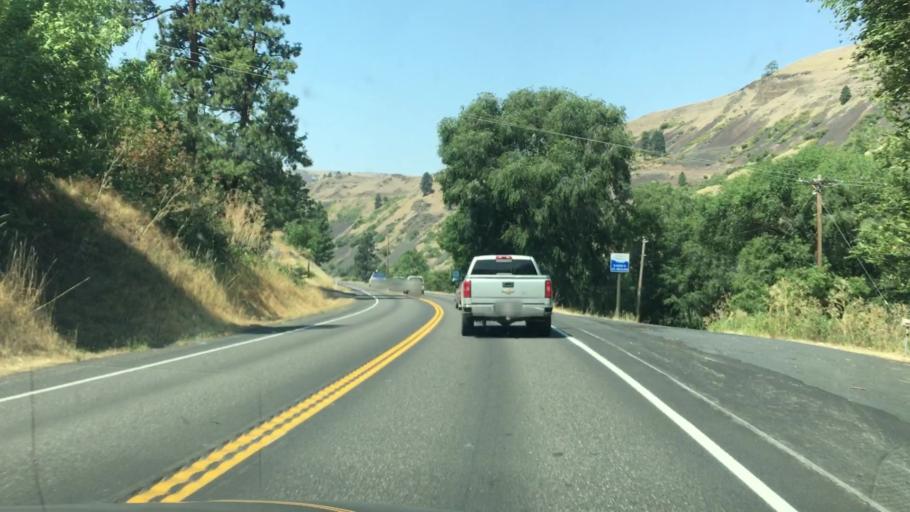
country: US
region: Idaho
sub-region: Nez Perce County
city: Lapwai
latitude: 46.4879
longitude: -116.7447
